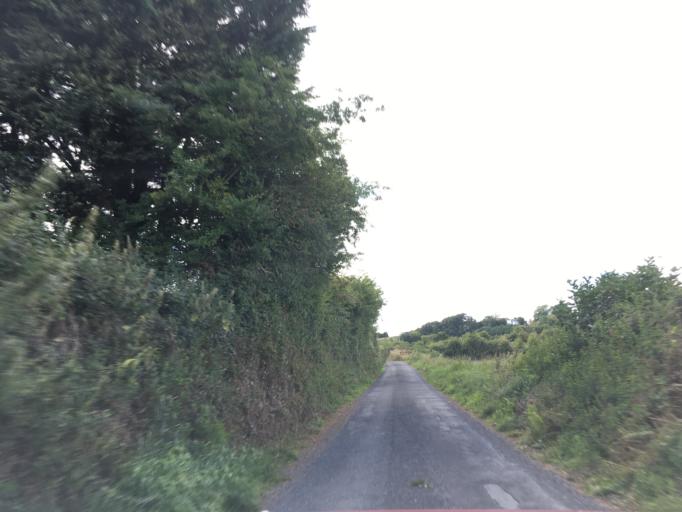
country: IE
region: Munster
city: Cashel
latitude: 52.5202
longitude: -7.8741
